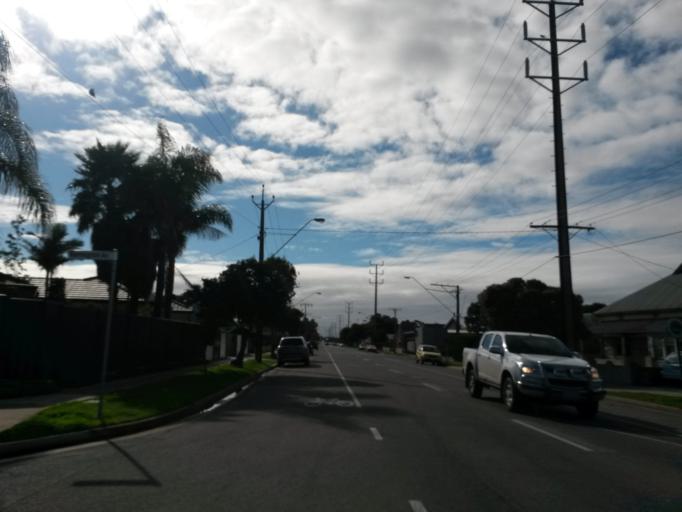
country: AU
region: South Australia
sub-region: Charles Sturt
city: West Lakes Shore
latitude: -34.8500
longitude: 138.4847
